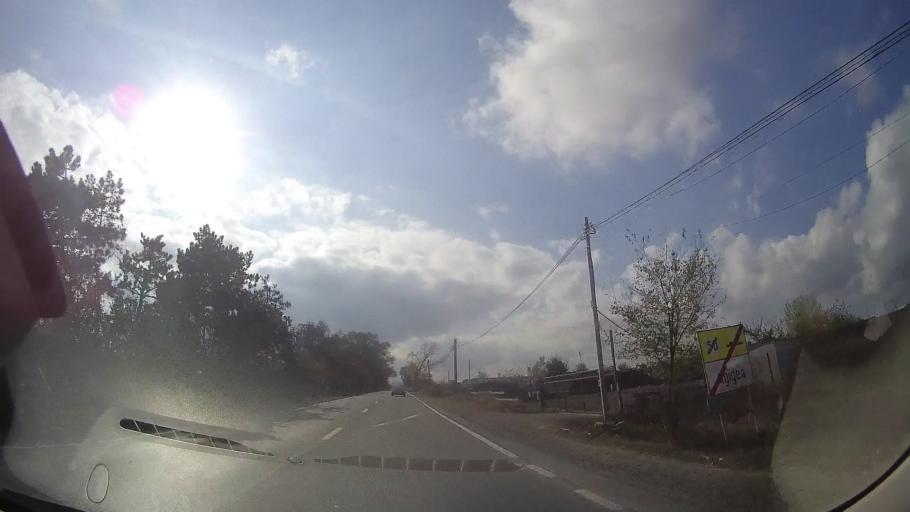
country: RO
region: Constanta
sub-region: Comuna Agigea
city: Agigea
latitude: 44.0855
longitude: 28.6077
